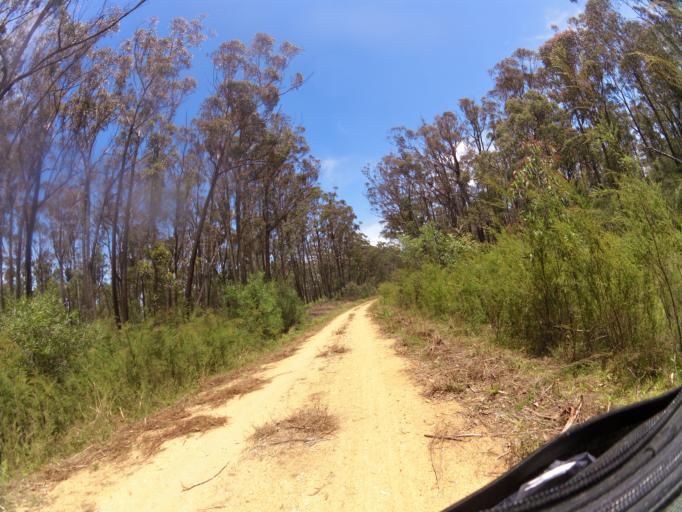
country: AU
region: Victoria
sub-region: East Gippsland
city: Lakes Entrance
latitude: -37.7549
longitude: 147.9699
